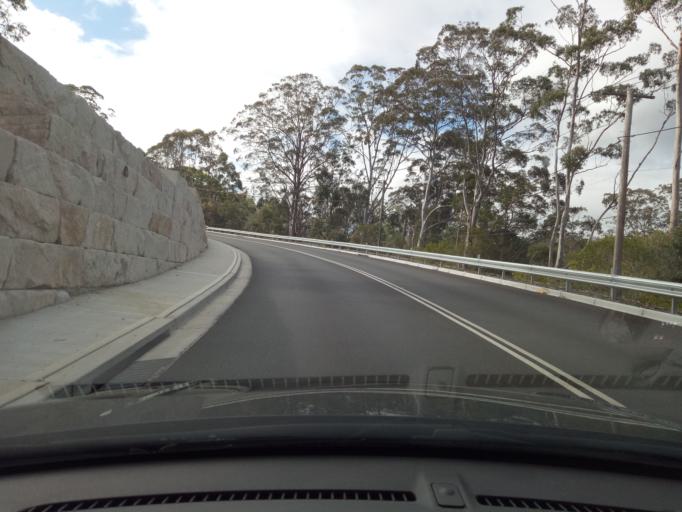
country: AU
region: New South Wales
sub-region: Gosford Shire
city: Lisarow
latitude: -33.3899
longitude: 151.3822
